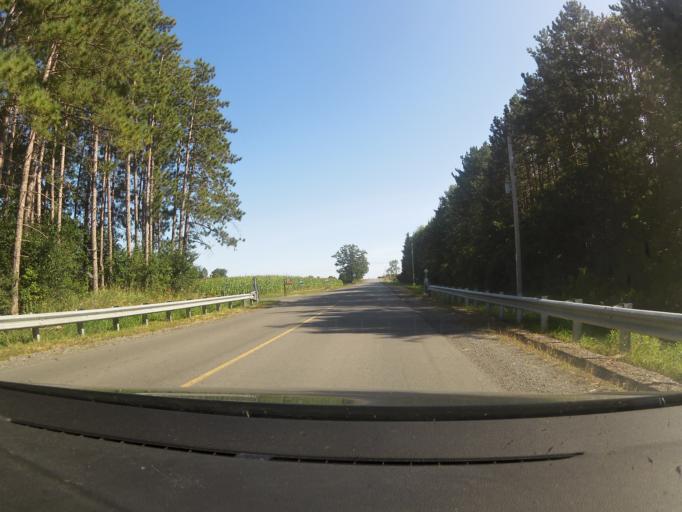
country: CA
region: Ontario
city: Arnprior
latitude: 45.4073
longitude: -76.1617
